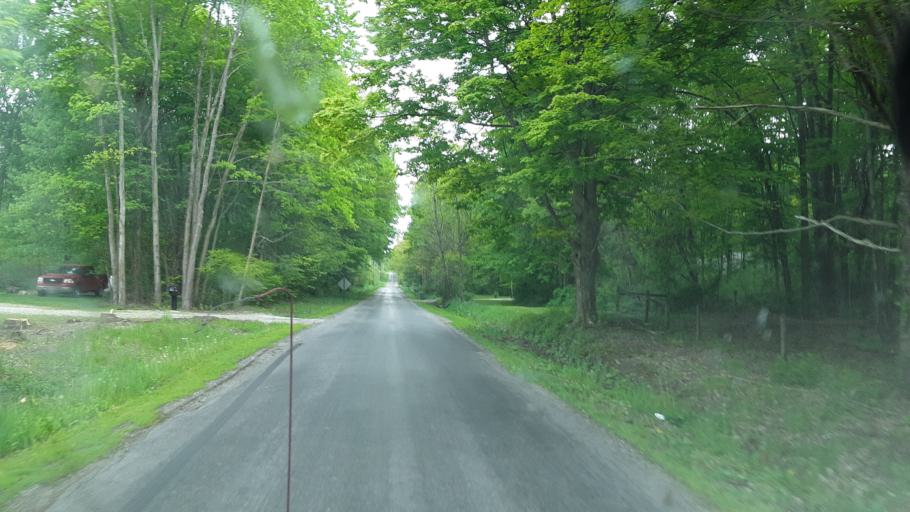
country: US
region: Ohio
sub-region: Portage County
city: Garrettsville
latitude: 41.3094
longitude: -81.0388
